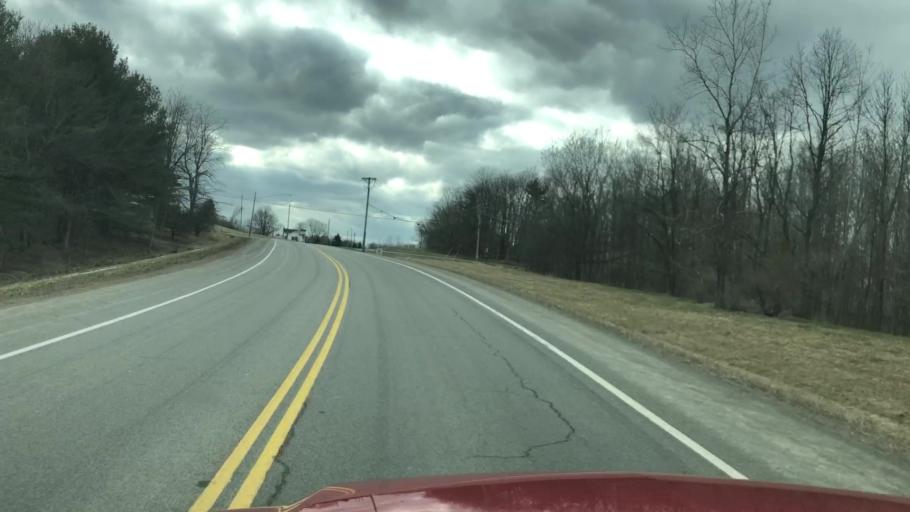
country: US
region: New York
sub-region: Wayne County
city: Macedon
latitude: 43.1281
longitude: -77.3515
